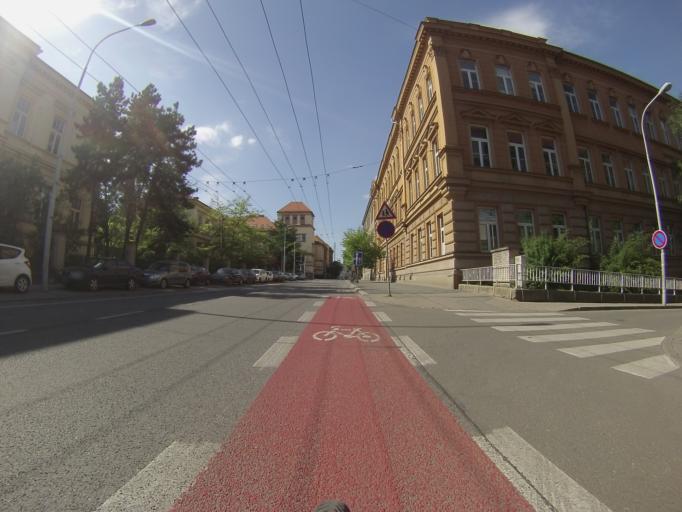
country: CZ
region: South Moravian
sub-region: Mesto Brno
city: Brno
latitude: 49.2048
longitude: 16.5984
